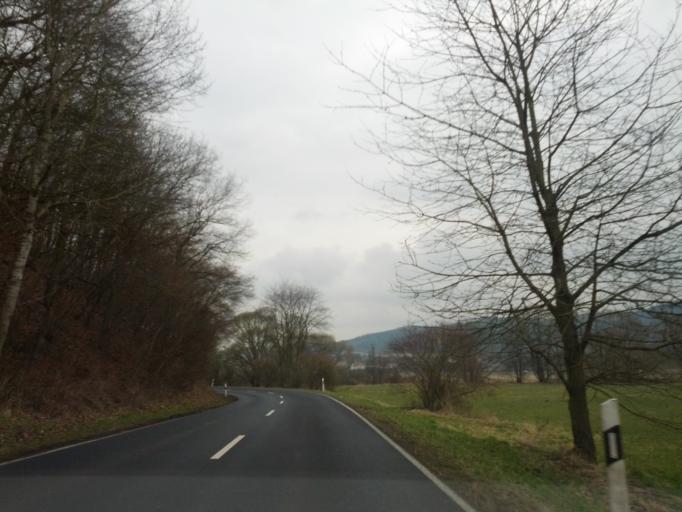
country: DE
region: Hesse
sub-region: Regierungsbezirk Kassel
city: Herleshausen
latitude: 50.9969
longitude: 10.1857
